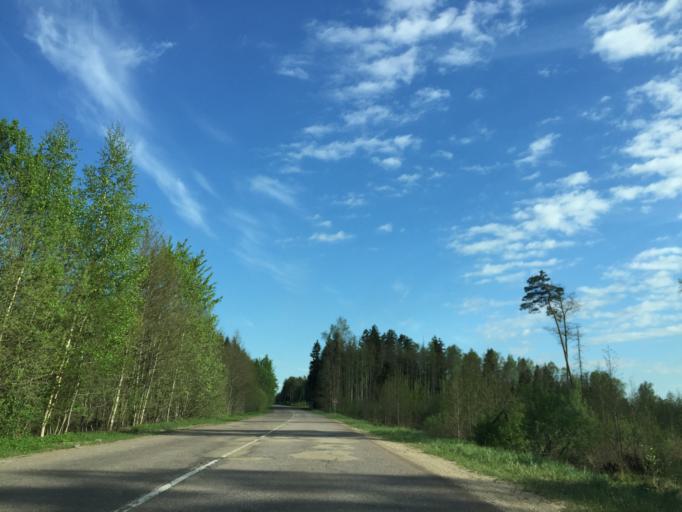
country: LV
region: Lecava
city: Iecava
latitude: 56.6982
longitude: 24.1152
